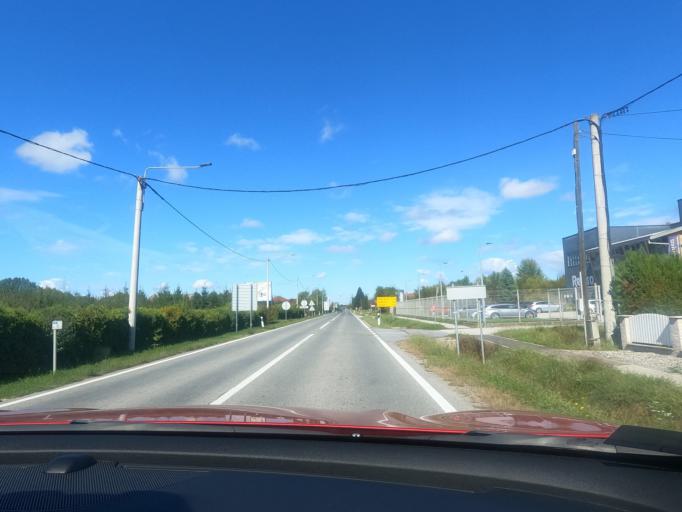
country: HR
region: Sisacko-Moslavacka
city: Lekenik
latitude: 45.5706
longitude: 16.2241
